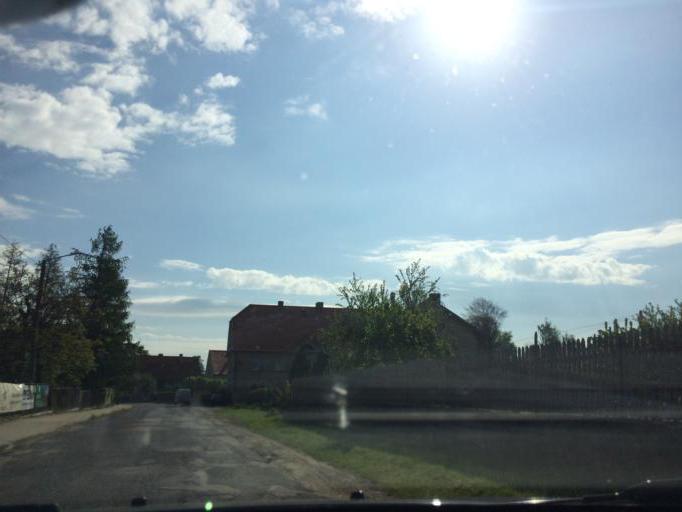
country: PL
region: Lower Silesian Voivodeship
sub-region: Powiat dzierzoniowski
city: Pieszyce
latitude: 50.7515
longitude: 16.5233
